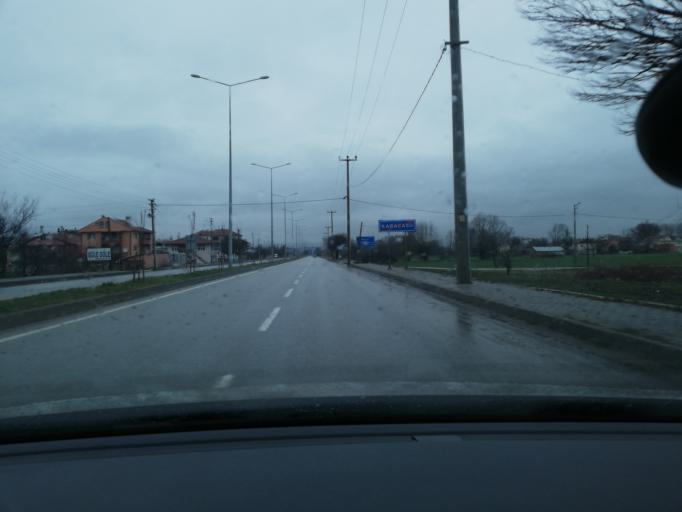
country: TR
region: Bolu
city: Bolu
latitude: 40.6952
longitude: 31.6194
